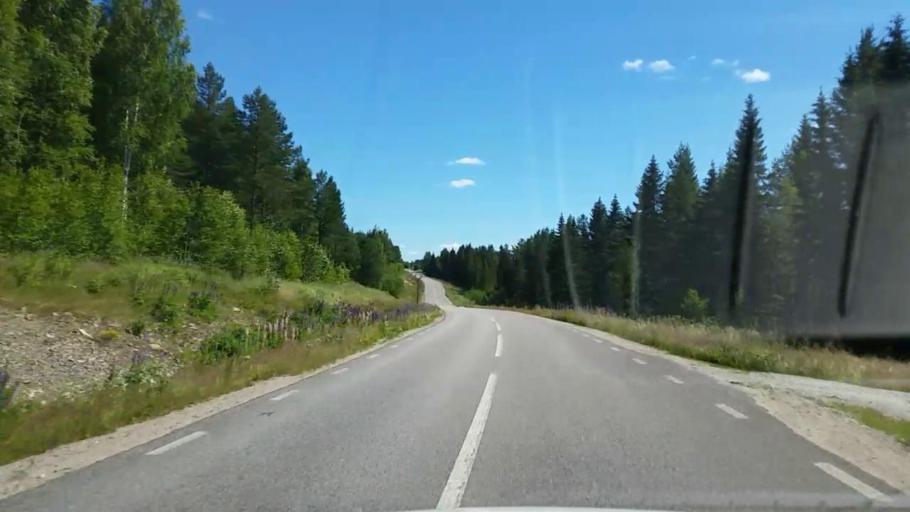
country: SE
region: Gaevleborg
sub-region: Ovanakers Kommun
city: Edsbyn
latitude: 61.5979
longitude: 15.5543
